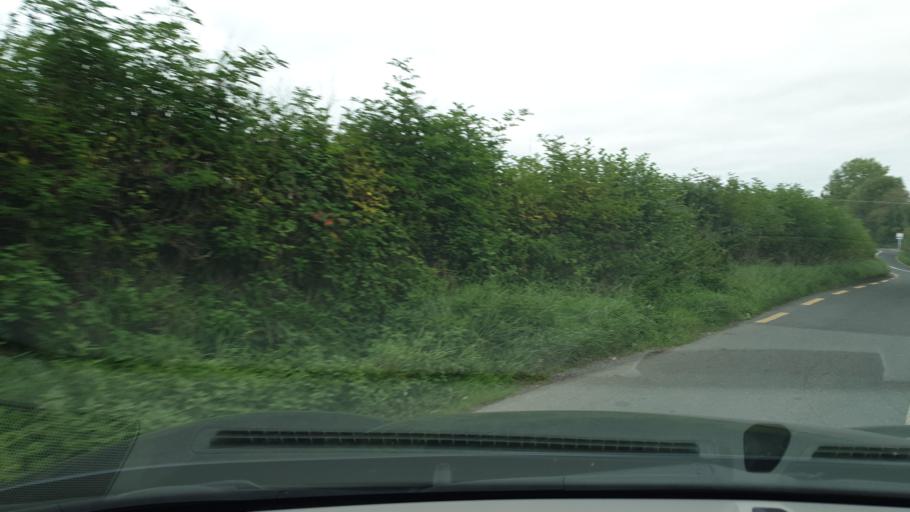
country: IE
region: Leinster
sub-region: Kildare
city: Kilcock
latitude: 53.4096
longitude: -6.6672
